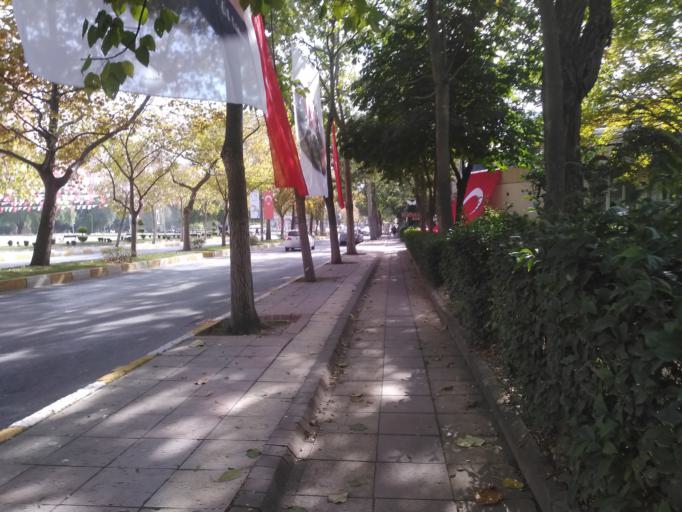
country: TR
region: Istanbul
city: Beylikduezue
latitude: 41.0058
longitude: 28.6434
